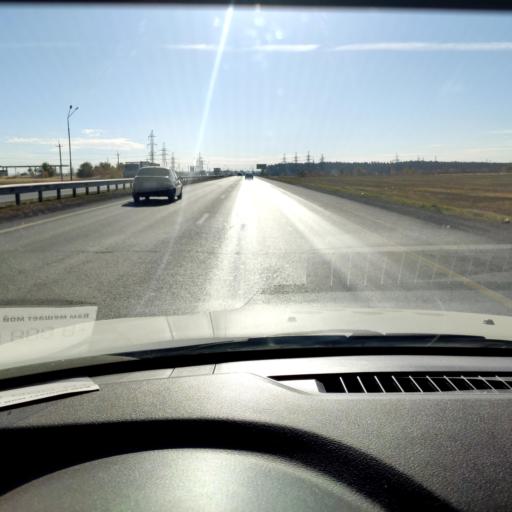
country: RU
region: Samara
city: Zhigulevsk
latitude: 53.5484
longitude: 49.5092
